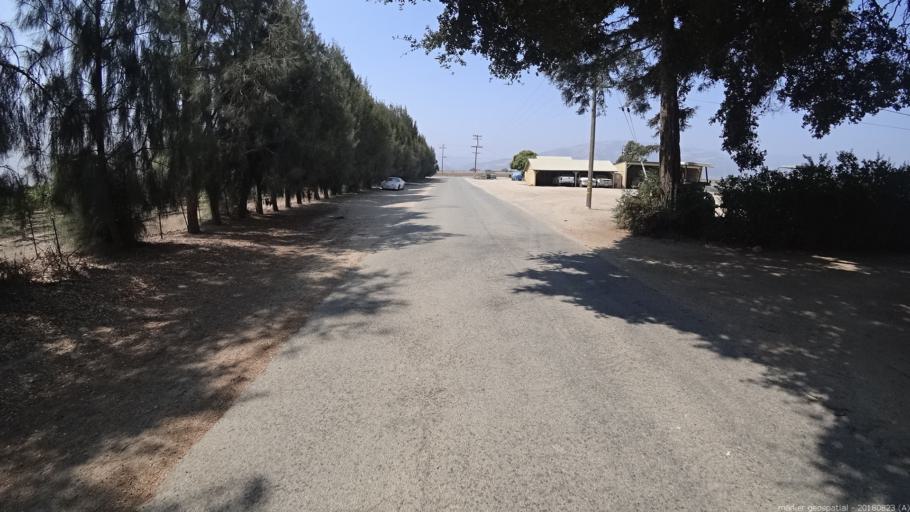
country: US
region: California
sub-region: Monterey County
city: Greenfield
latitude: 36.3091
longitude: -121.2644
